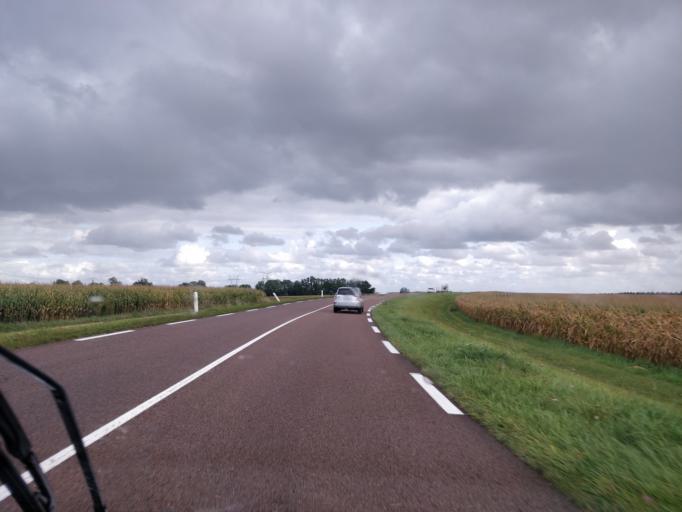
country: FR
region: Champagne-Ardenne
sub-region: Departement de l'Aube
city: Verrieres
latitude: 48.2790
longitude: 4.1962
